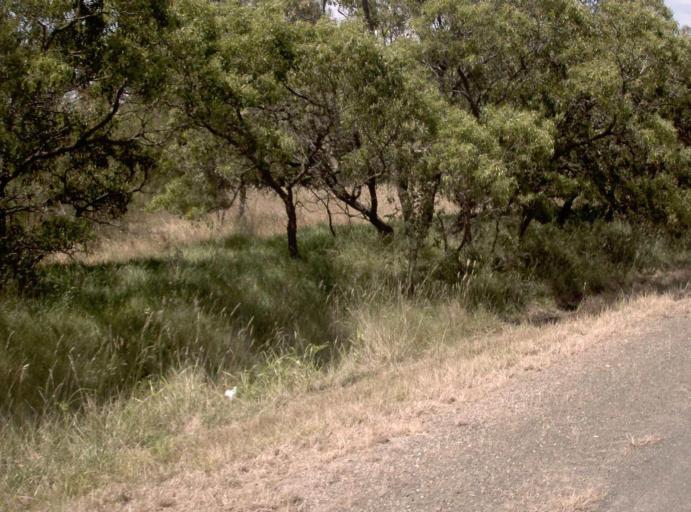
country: AU
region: Victoria
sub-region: Wellington
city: Sale
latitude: -38.1039
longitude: 146.9255
